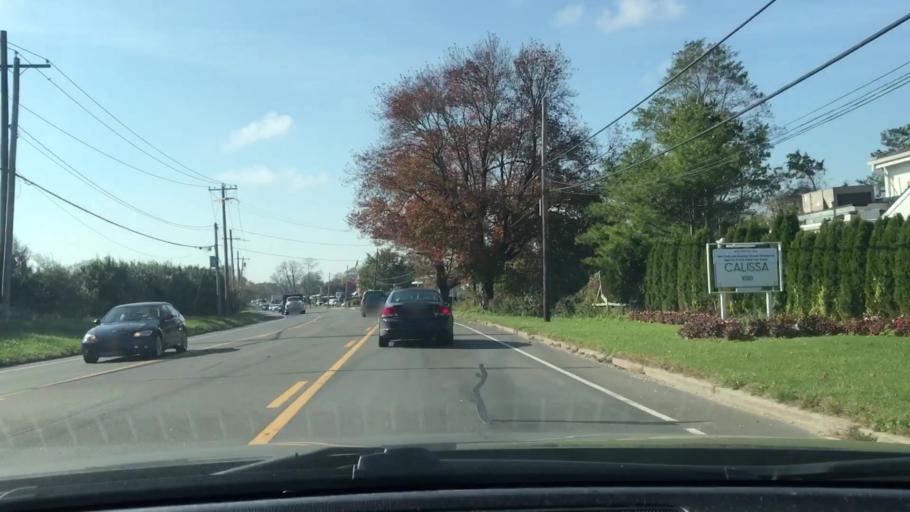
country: US
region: New York
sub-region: Suffolk County
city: Water Mill
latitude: 40.9166
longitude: -72.3461
